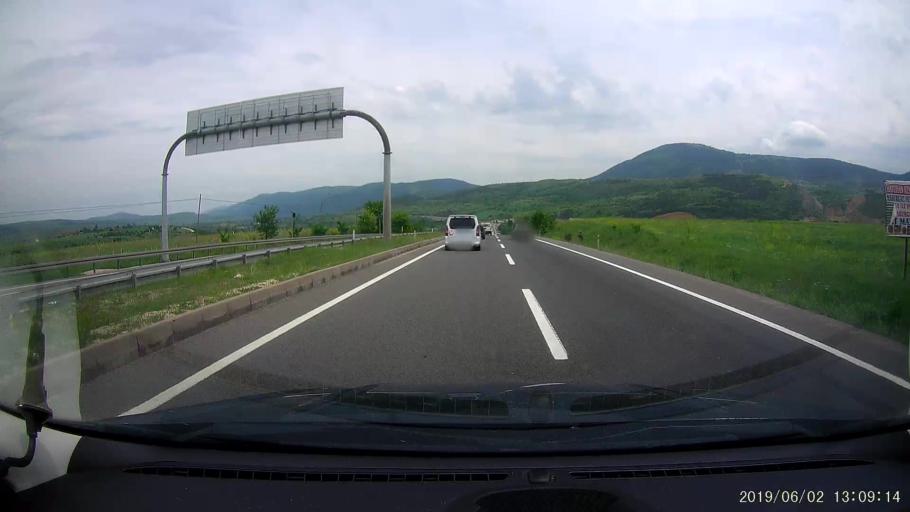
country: TR
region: Karabuk
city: Gozyeri
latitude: 40.8708
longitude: 32.5848
